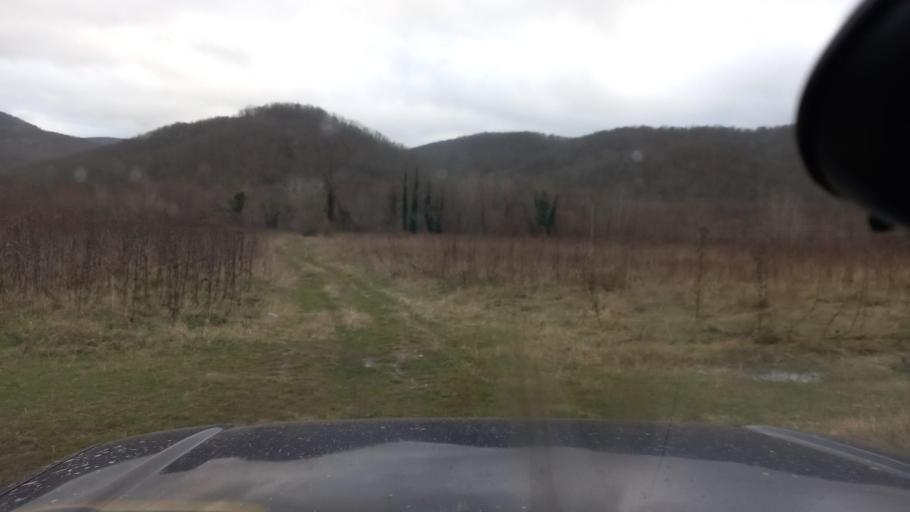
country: RU
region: Krasnodarskiy
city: Pshada
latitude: 44.4930
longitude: 38.4127
